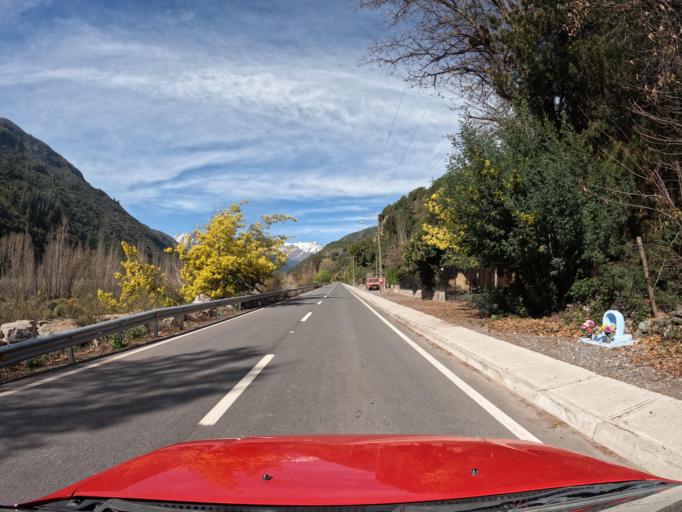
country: CL
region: O'Higgins
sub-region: Provincia de Colchagua
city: Chimbarongo
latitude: -35.0000
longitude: -70.8074
